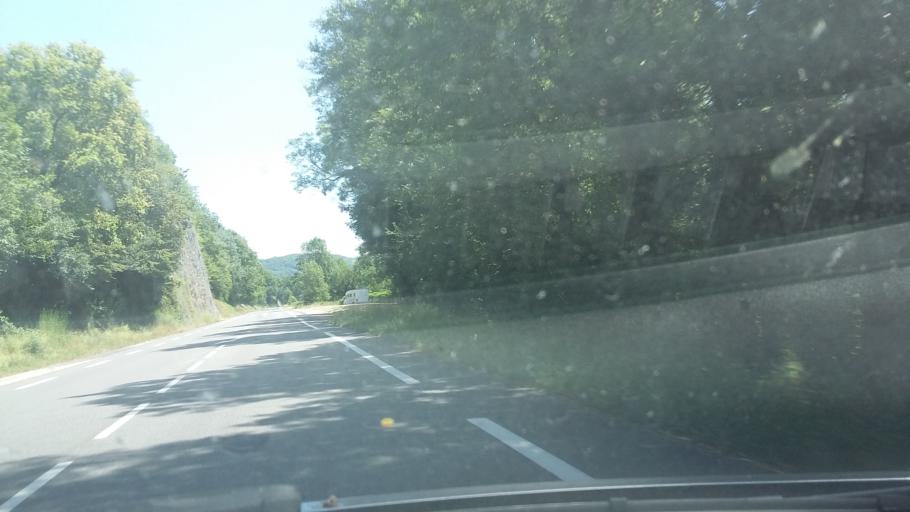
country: FR
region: Rhone-Alpes
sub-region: Departement de l'Ain
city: Virieu-le-Grand
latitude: 45.8137
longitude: 5.6603
